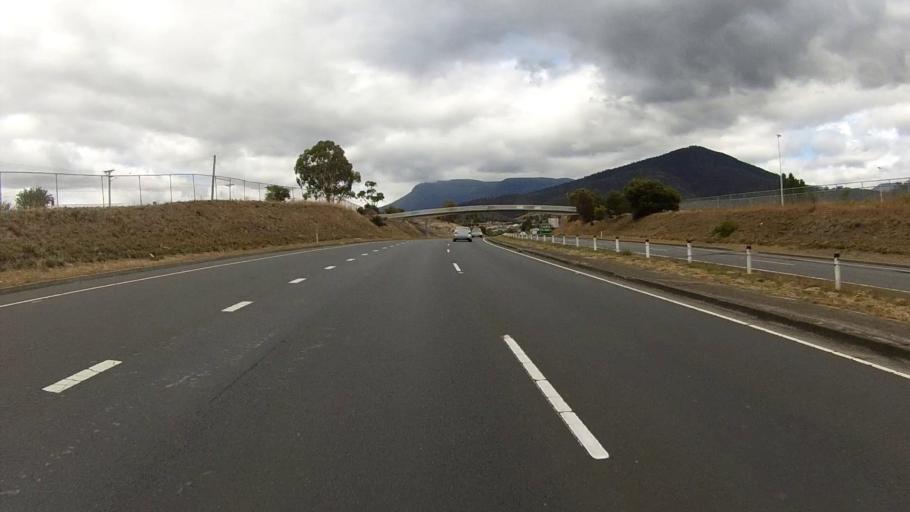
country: AU
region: Tasmania
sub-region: Glenorchy
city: Berriedale
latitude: -42.8031
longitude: 147.2499
